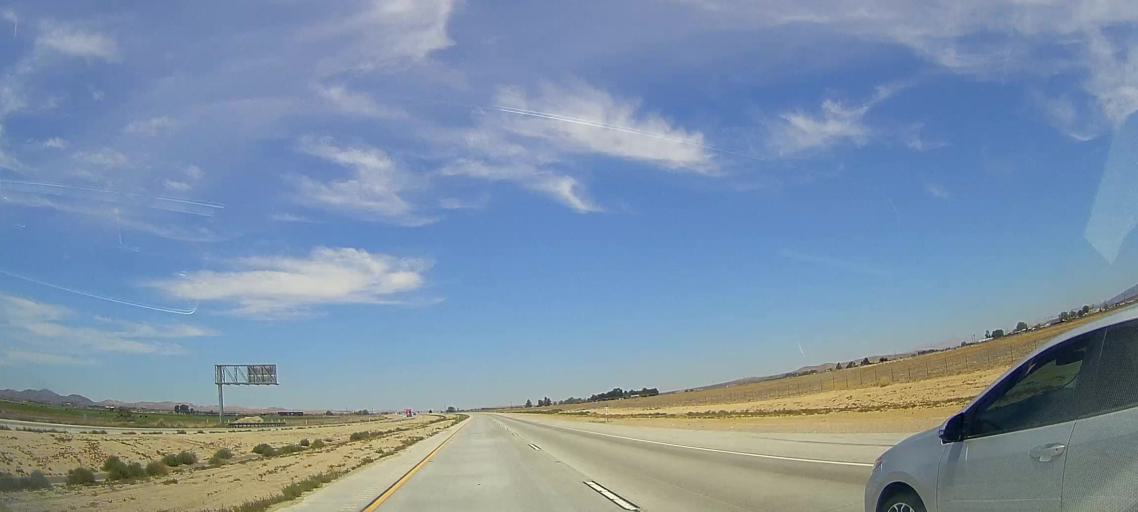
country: US
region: California
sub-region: San Bernardino County
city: Lenwood
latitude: 34.9152
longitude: -117.1259
